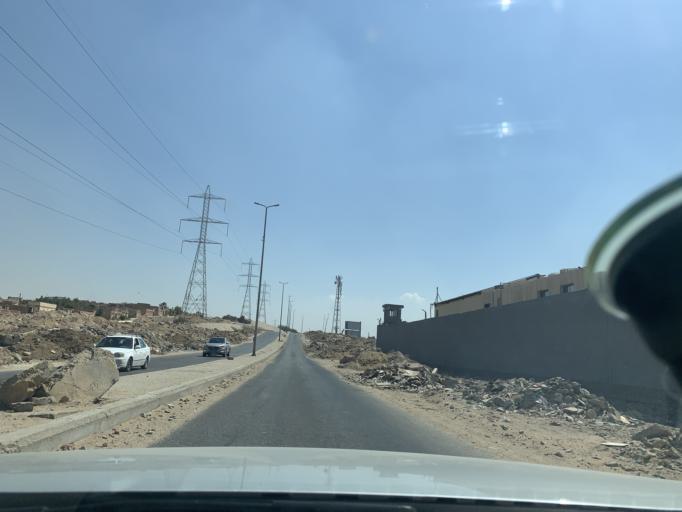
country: EG
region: Muhafazat al Qahirah
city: Cairo
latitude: 30.0266
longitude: 31.3464
